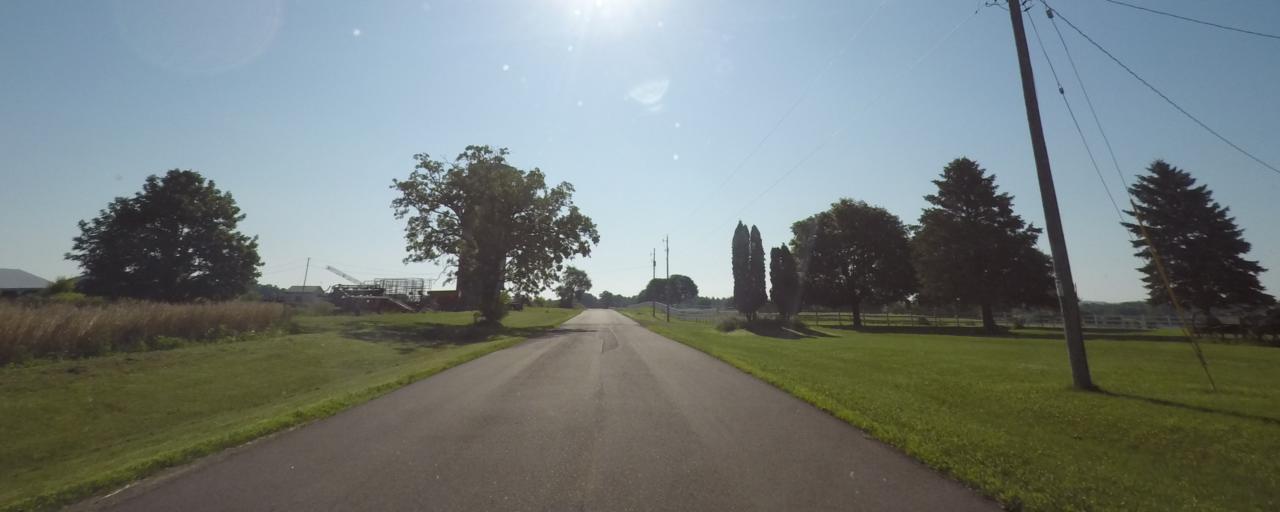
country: US
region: Wisconsin
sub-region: Jefferson County
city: Palmyra
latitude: 42.9189
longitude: -88.5560
